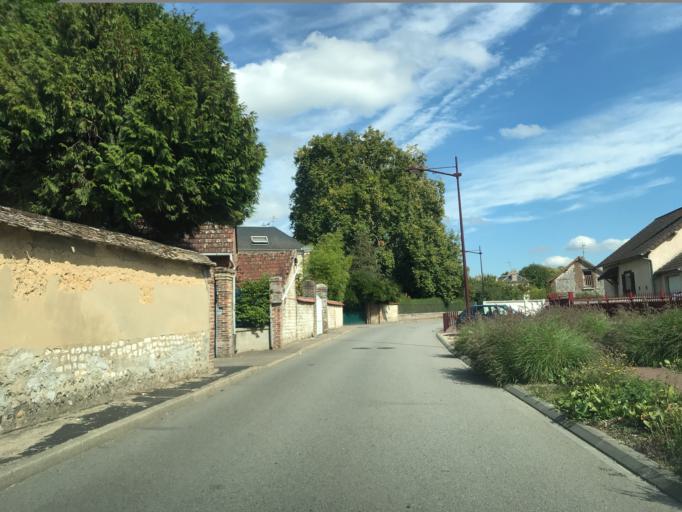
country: FR
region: Haute-Normandie
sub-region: Departement de l'Eure
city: Le Vaudreuil
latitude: 49.2548
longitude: 1.2014
